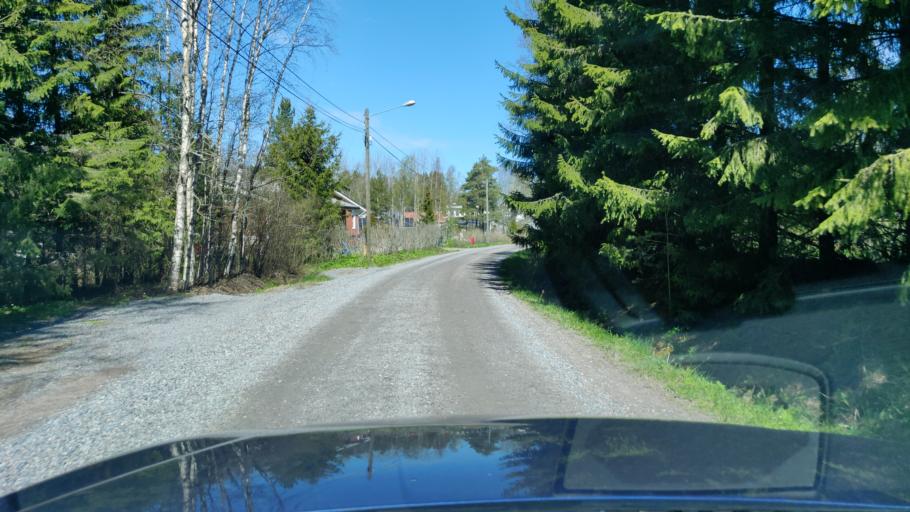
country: FI
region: Uusimaa
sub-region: Helsinki
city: Nurmijaervi
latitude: 60.3595
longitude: 24.7563
